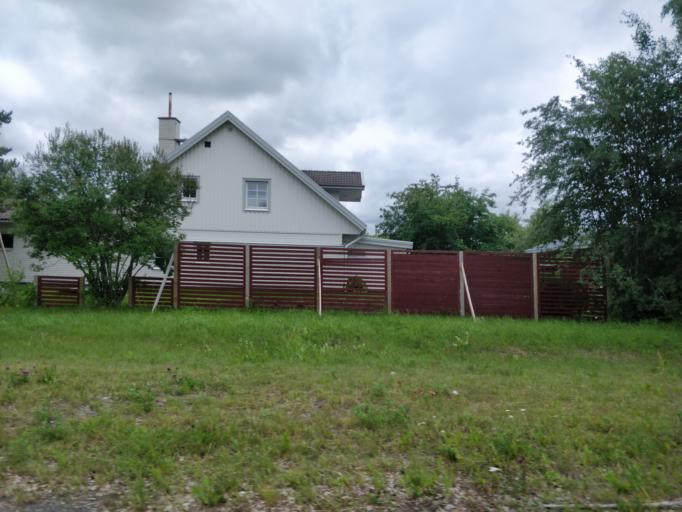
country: SE
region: Vaesterbotten
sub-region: Skelleftea Kommun
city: Viken
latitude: 64.7578
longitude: 20.8923
